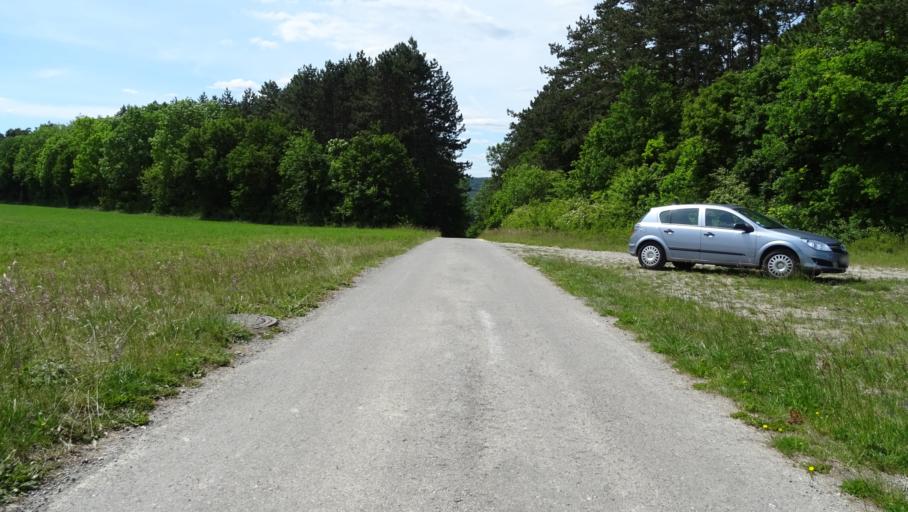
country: DE
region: Baden-Wuerttemberg
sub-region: Karlsruhe Region
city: Seckach
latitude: 49.4786
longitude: 9.3262
